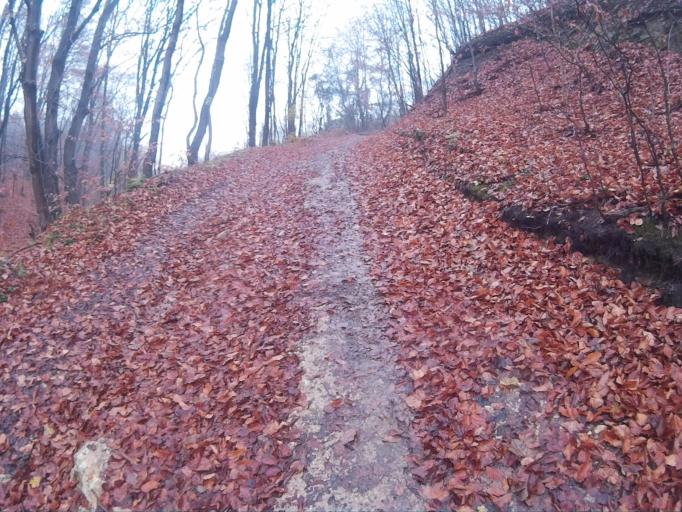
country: HU
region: Veszprem
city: Herend
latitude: 47.2564
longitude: 17.7388
